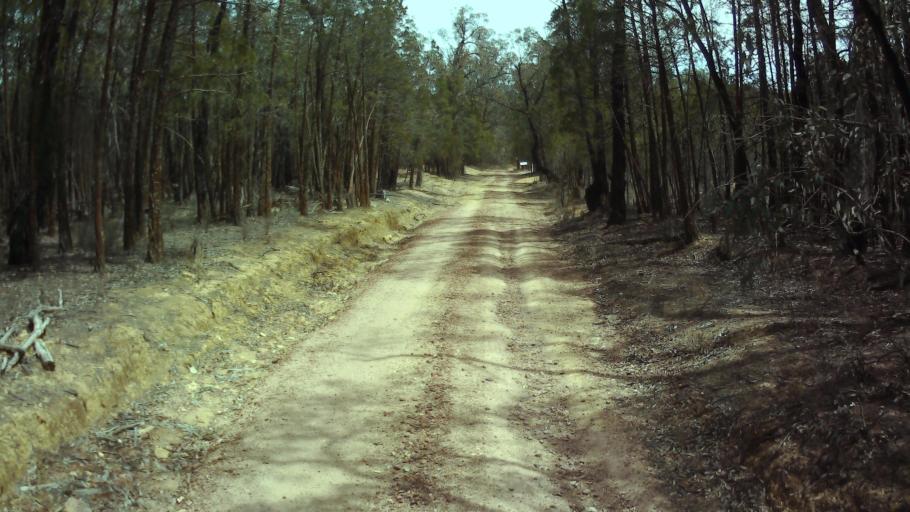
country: AU
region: New South Wales
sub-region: Weddin
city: Grenfell
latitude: -33.8929
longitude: 148.3896
